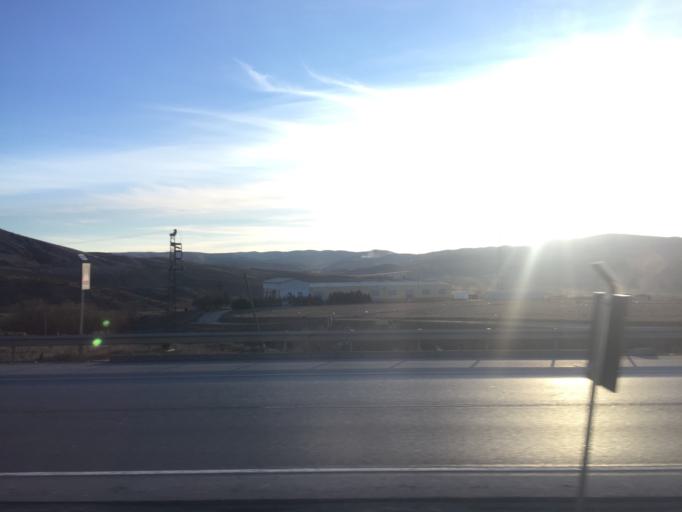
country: TR
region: Kirikkale
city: Yahsihan
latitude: 39.8808
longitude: 33.4381
